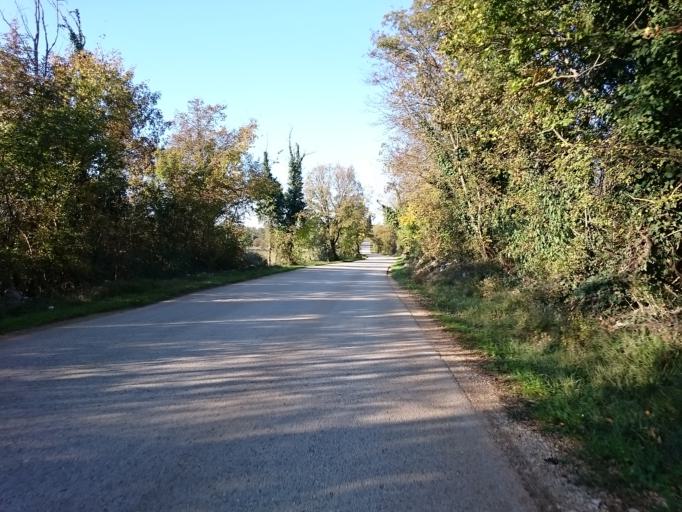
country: HR
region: Istarska
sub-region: Grad Porec
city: Porec
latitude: 45.2857
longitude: 13.6428
